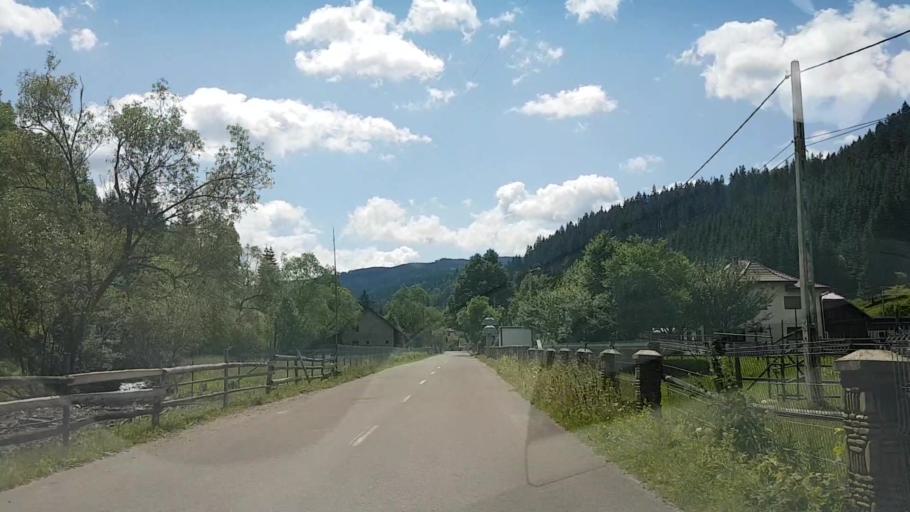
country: RO
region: Suceava
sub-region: Comuna Pojorata
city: Pojorata
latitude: 47.4920
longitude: 25.4853
